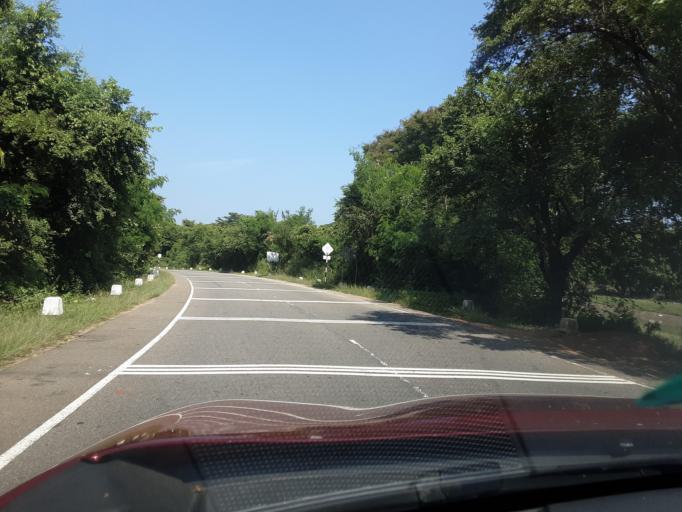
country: LK
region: Uva
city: Badulla
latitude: 7.2821
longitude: 81.0441
